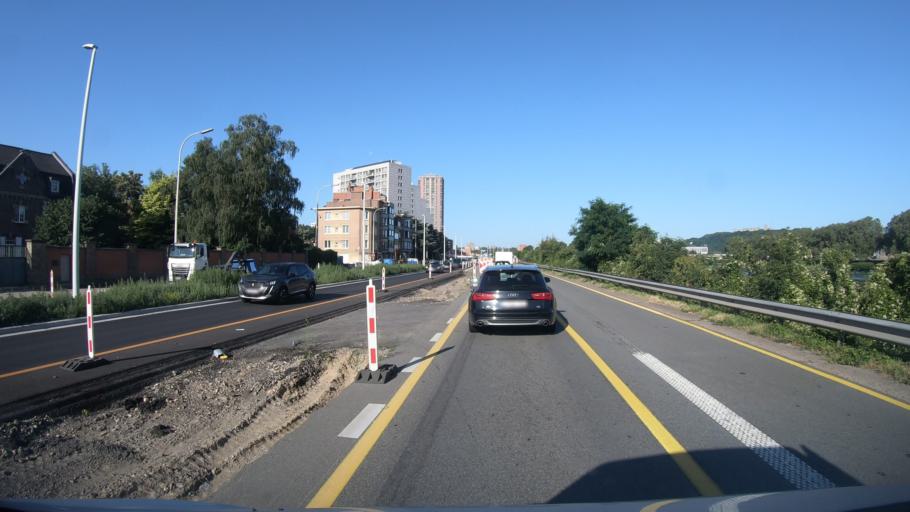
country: BE
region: Wallonia
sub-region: Province de Liege
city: Herstal
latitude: 50.6537
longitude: 5.6033
